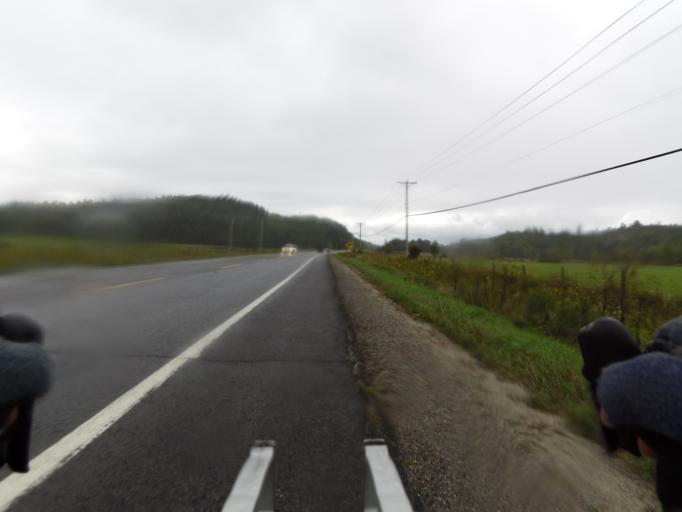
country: CA
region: Quebec
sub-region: Outaouais
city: Wakefield
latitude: 45.6437
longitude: -75.8963
